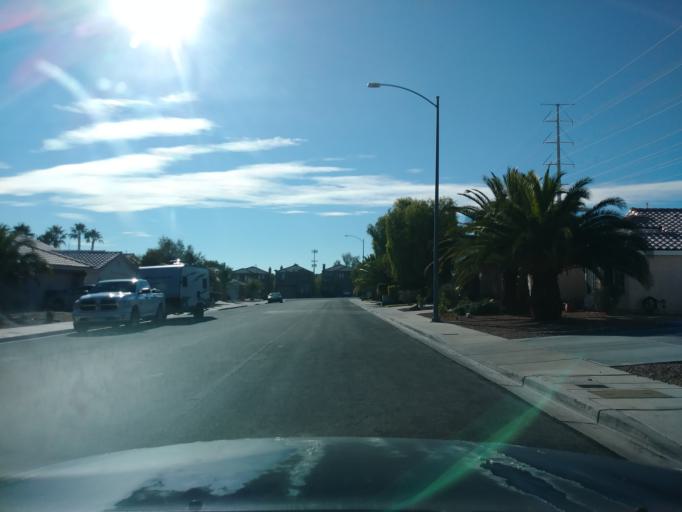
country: US
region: Nevada
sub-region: Clark County
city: Spring Valley
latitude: 36.1489
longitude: -115.2788
